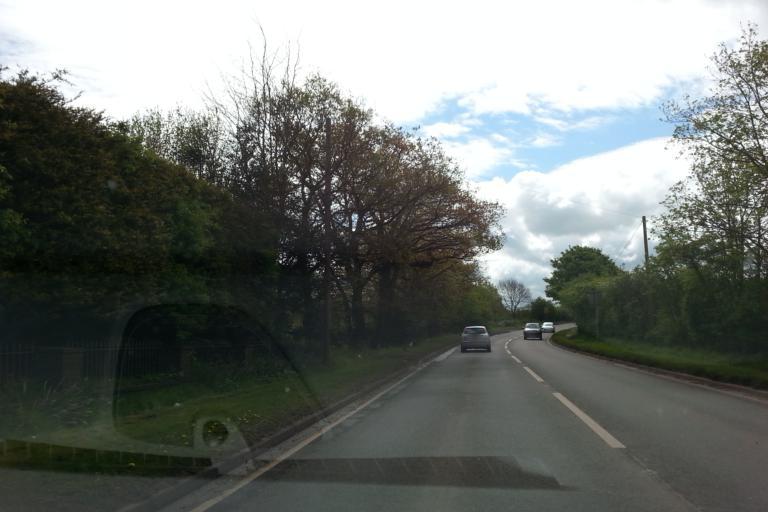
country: GB
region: England
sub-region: Staffordshire
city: Essington
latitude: 52.6479
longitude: -2.0461
